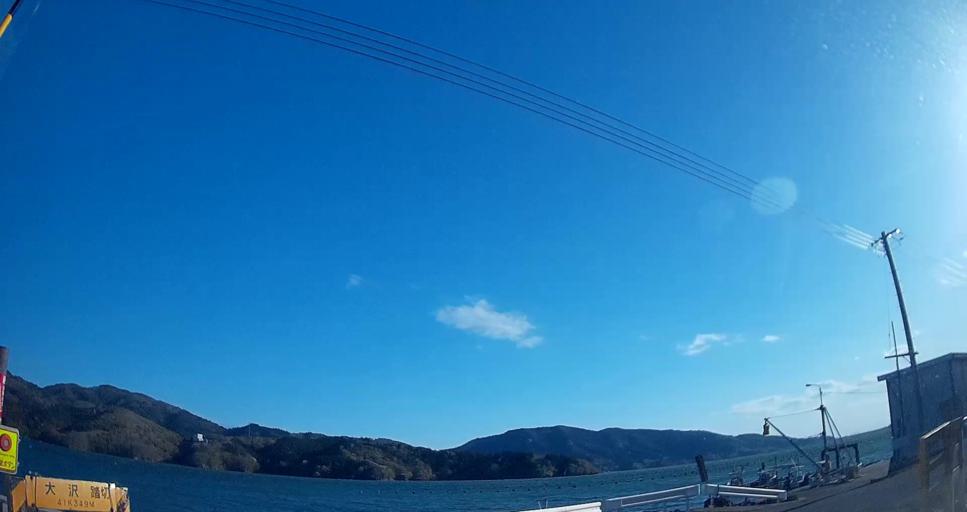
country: JP
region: Miyagi
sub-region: Oshika Gun
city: Onagawa Cho
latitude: 38.4335
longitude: 141.4113
